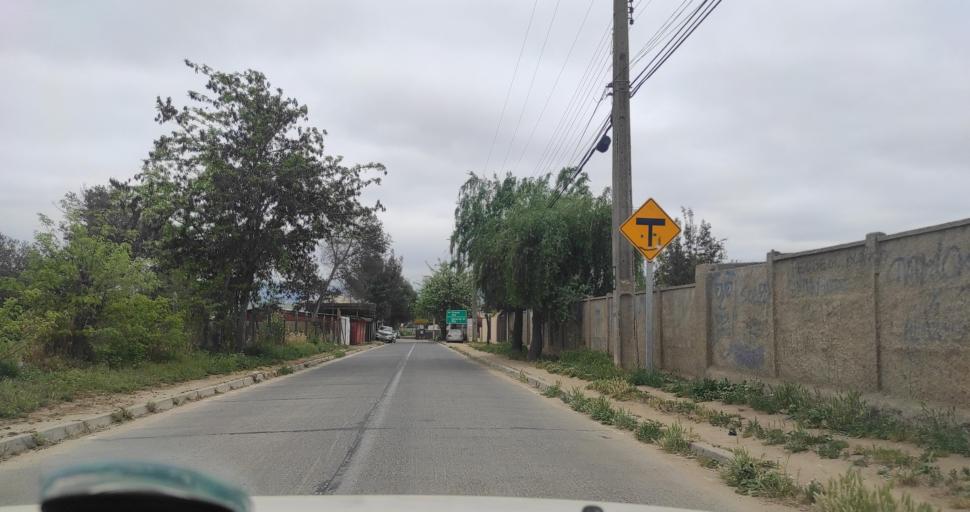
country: CL
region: Valparaiso
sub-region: Provincia de Marga Marga
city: Limache
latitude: -32.9952
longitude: -71.2263
